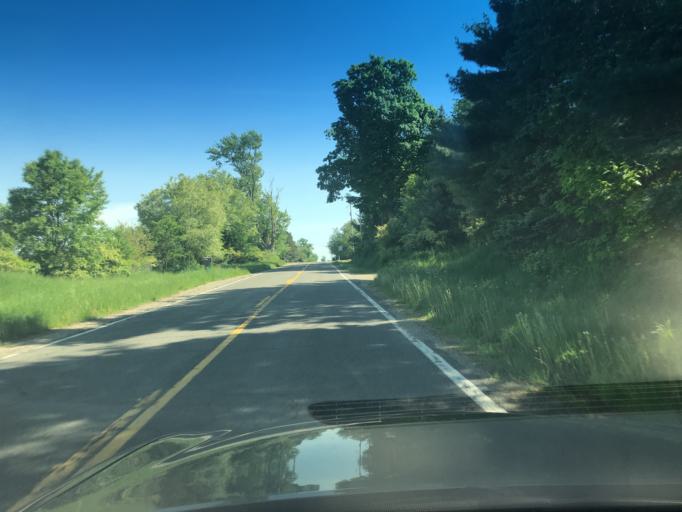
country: US
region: Michigan
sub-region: Ingham County
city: Mason
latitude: 42.5398
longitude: -84.4626
